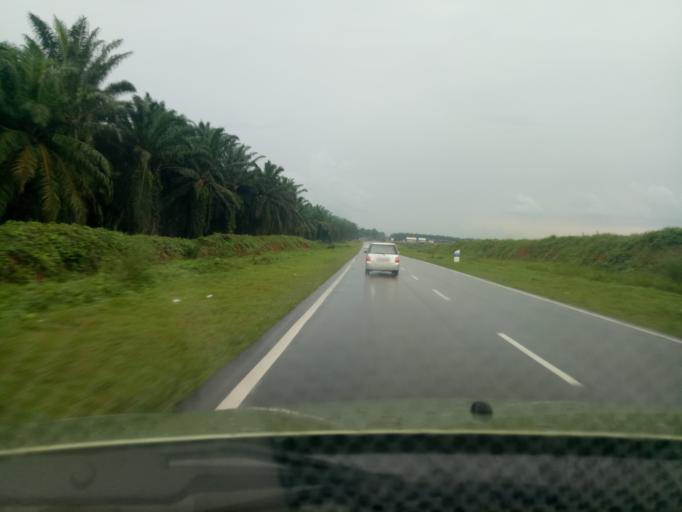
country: MY
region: Penang
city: Tasek Glugor
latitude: 5.5642
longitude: 100.5776
